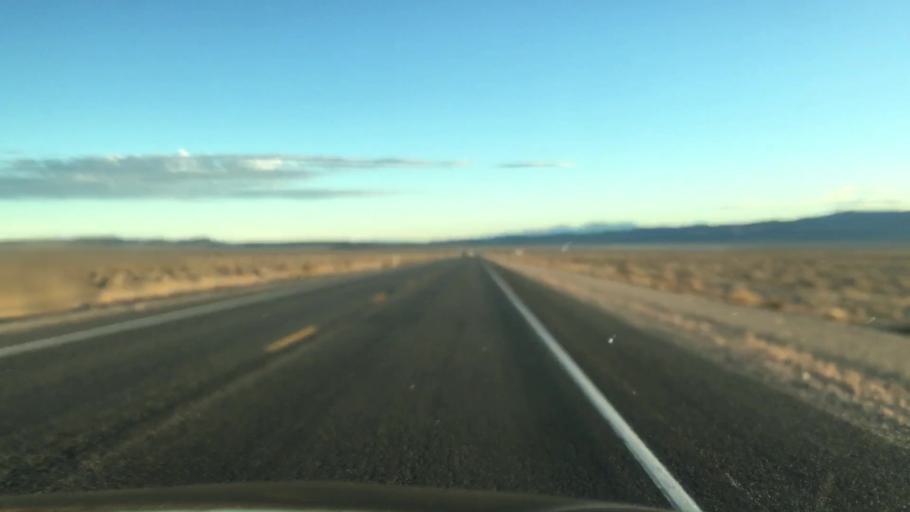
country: US
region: Nevada
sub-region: Esmeralda County
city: Goldfield
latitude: 37.5200
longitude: -117.1895
